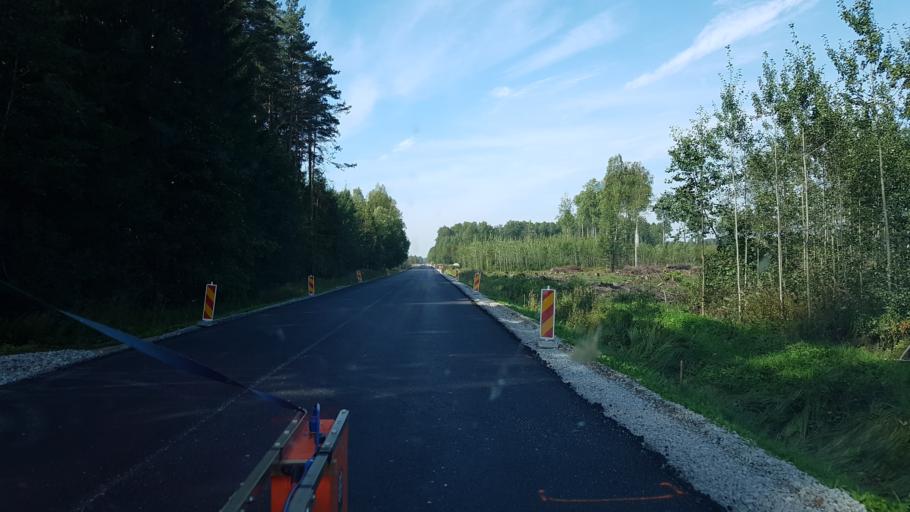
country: EE
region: Paernumaa
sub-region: Vaendra vald (alev)
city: Vandra
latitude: 58.8330
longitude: 25.0945
